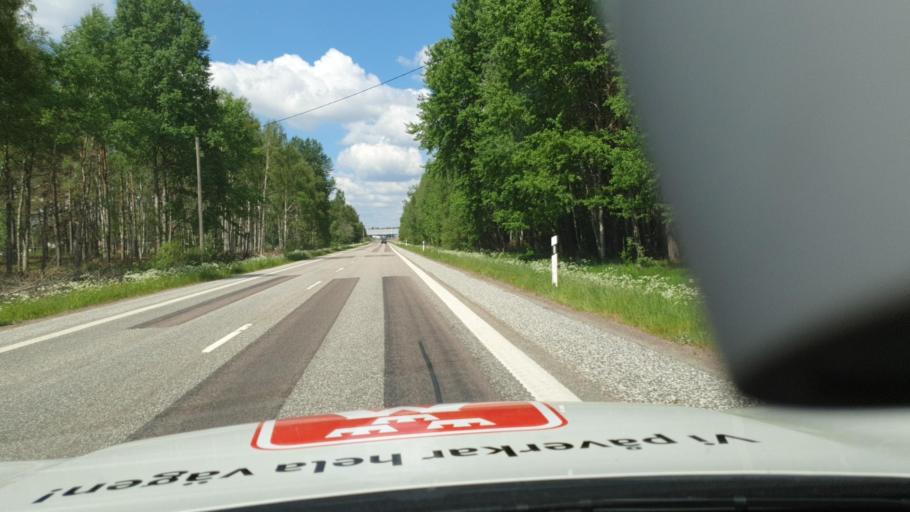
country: SE
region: Joenkoeping
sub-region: Jonkopings Kommun
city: Odensjo
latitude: 57.6422
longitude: 14.2019
